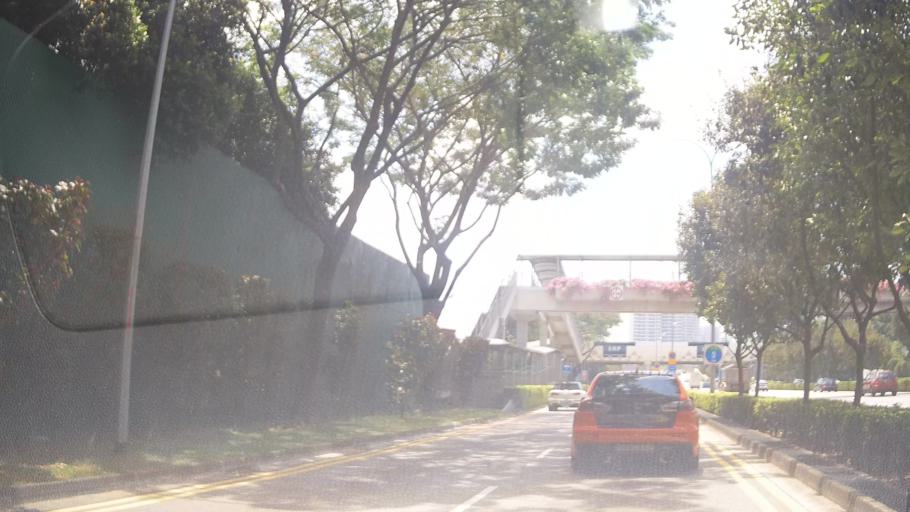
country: SG
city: Singapore
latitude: 1.3348
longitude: 103.8624
